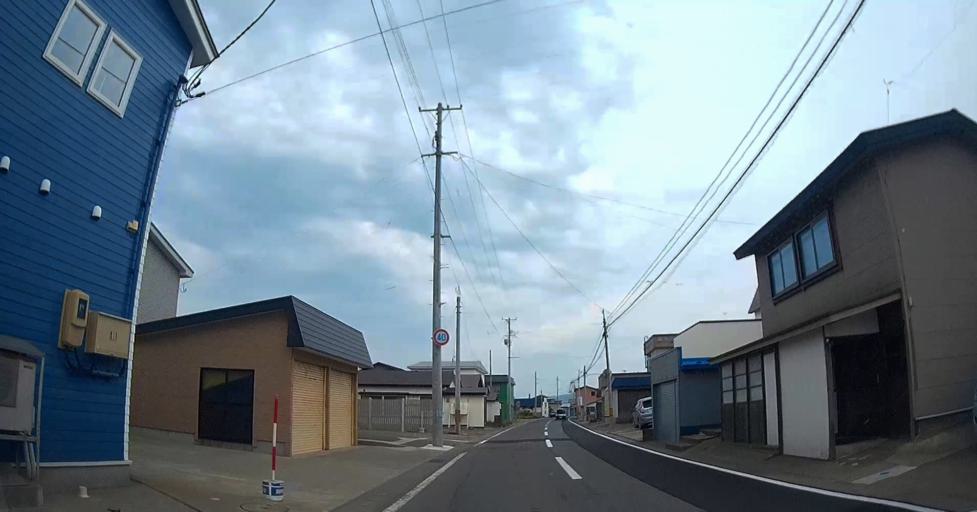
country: JP
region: Aomori
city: Shimokizukuri
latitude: 41.0286
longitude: 140.3259
